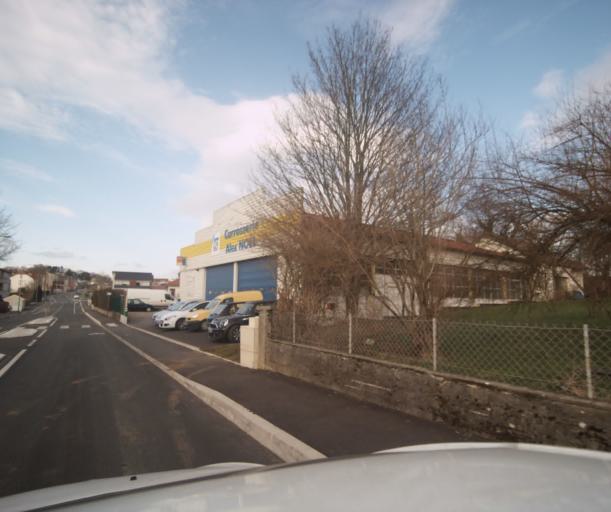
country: FR
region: Franche-Comte
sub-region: Departement du Doubs
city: Besancon
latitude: 47.2636
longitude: 6.0275
